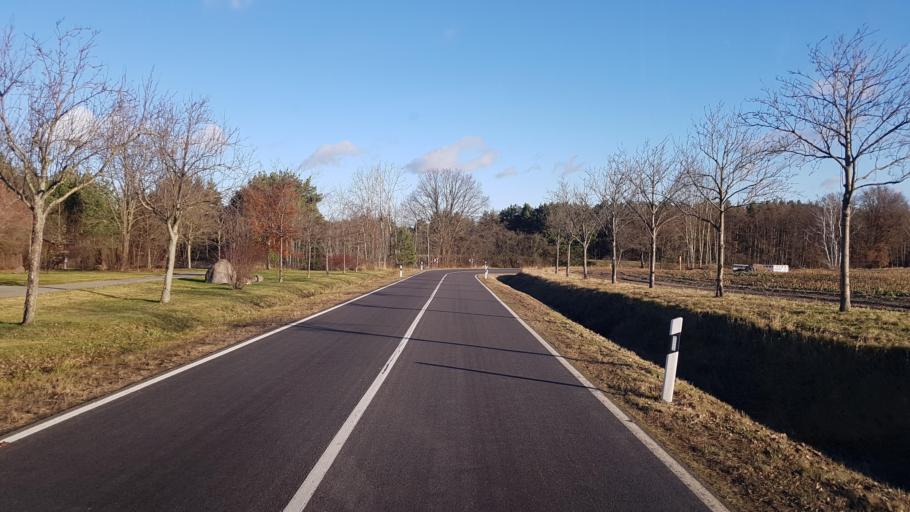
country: DE
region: Brandenburg
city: Forst
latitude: 51.7670
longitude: 14.5700
